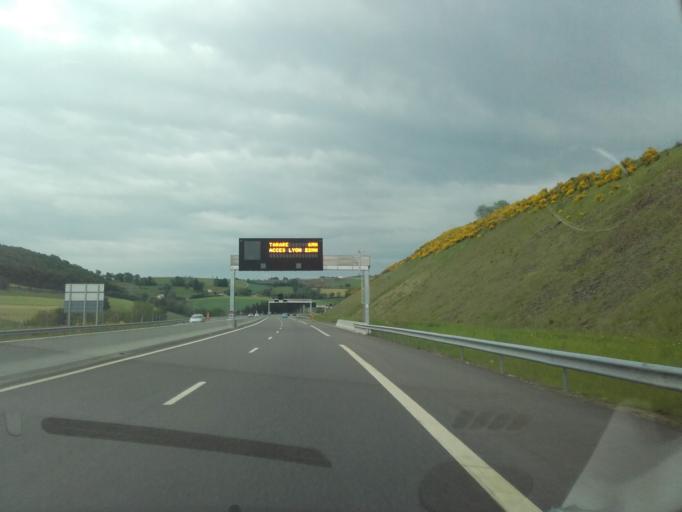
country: FR
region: Rhone-Alpes
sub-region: Departement de la Loire
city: Violay
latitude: 45.8623
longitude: 4.3125
